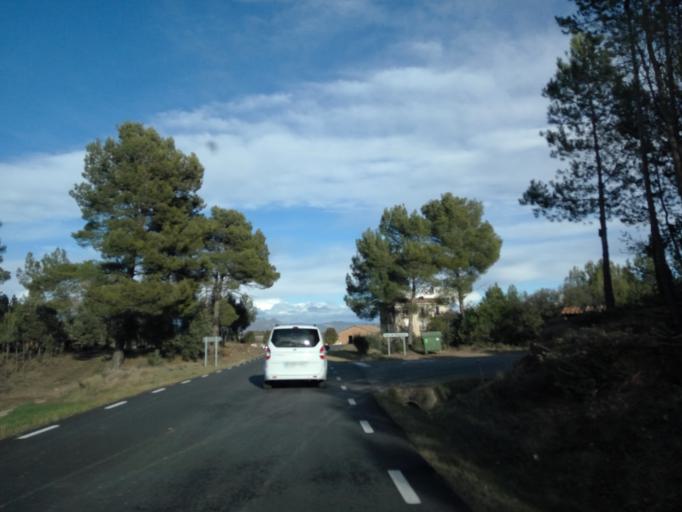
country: ES
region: Catalonia
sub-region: Provincia de Barcelona
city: Avia
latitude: 42.0237
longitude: 1.8008
